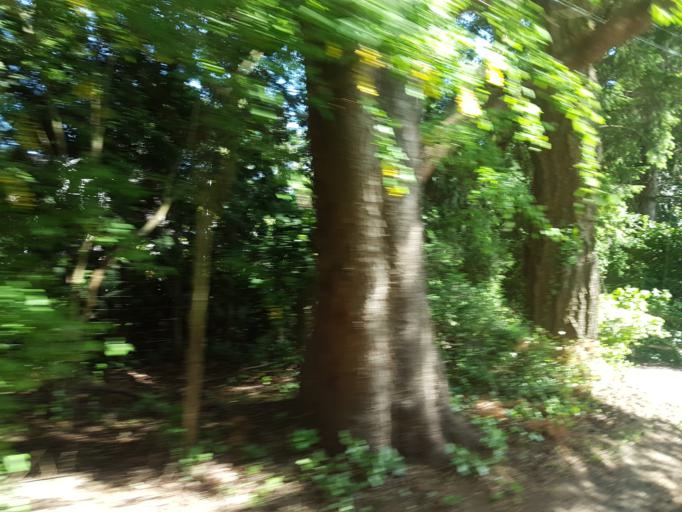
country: CA
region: British Columbia
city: Oak Bay
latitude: 48.4882
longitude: -123.3185
